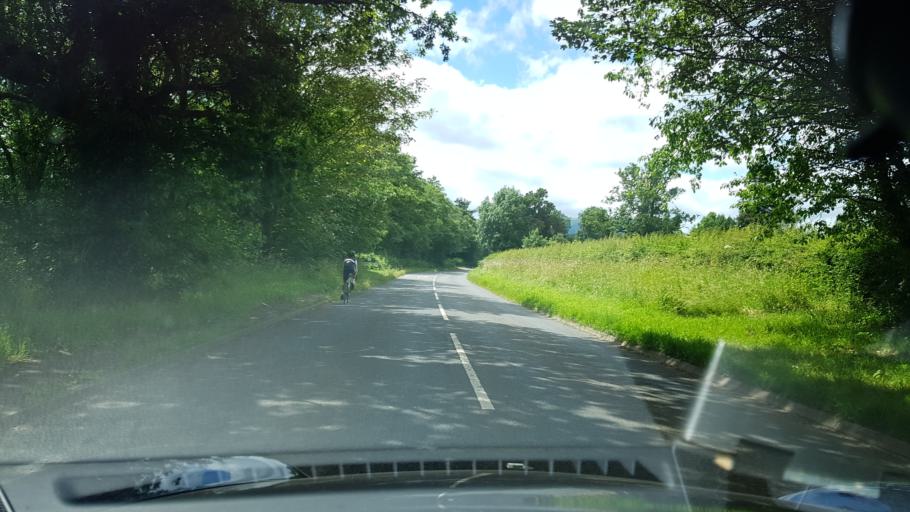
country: GB
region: Wales
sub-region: Monmouthshire
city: Llanarth
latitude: 51.7851
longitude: -2.9572
